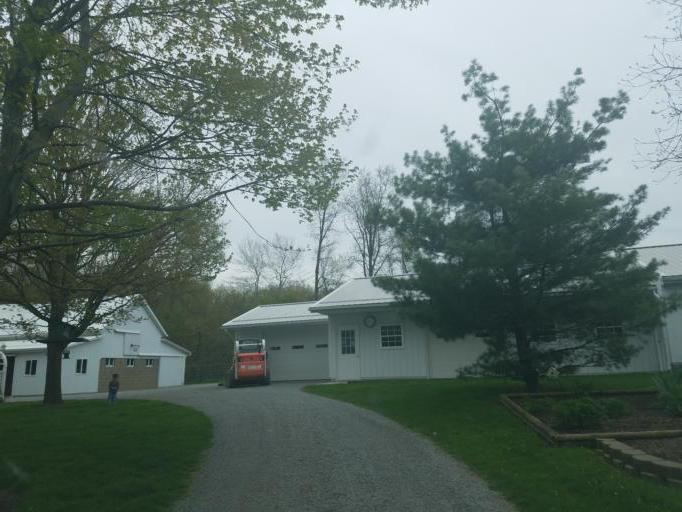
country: US
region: Ohio
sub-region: Wayne County
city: Apple Creek
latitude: 40.7262
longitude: -81.8160
